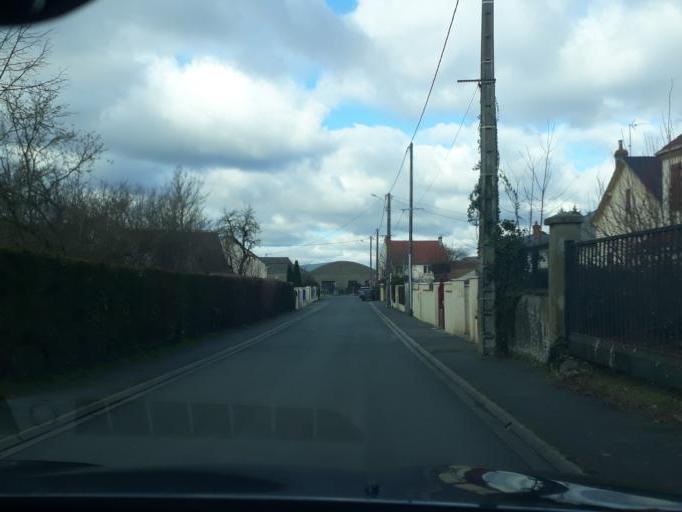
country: FR
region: Centre
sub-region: Departement du Loiret
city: Chevilly
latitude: 48.0306
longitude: 1.8769
